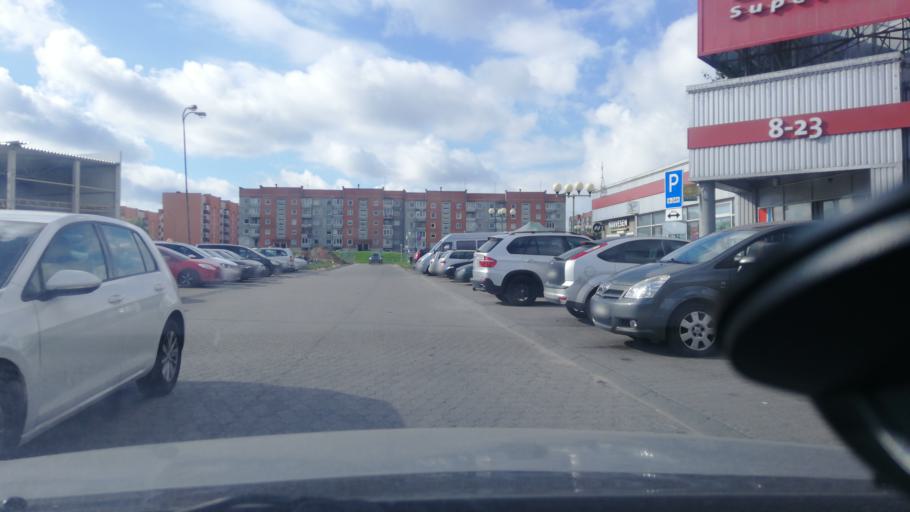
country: LT
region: Klaipedos apskritis
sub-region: Klaipeda
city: Klaipeda
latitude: 55.6674
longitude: 21.1974
